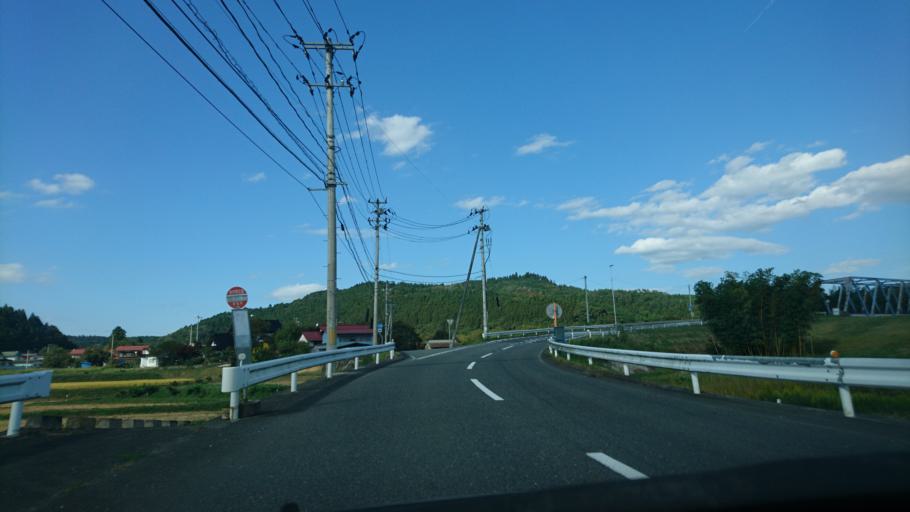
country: JP
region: Iwate
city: Ichinoseki
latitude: 38.8423
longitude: 141.2596
